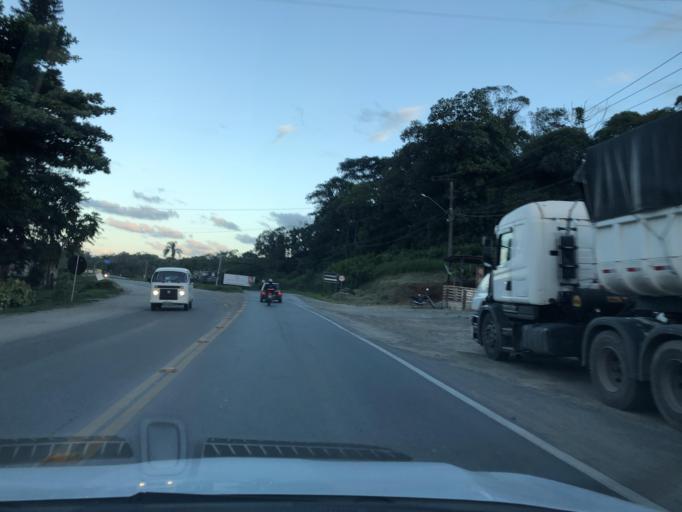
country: BR
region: Santa Catarina
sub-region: Sao Francisco Do Sul
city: Sao Francisco do Sul
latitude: -26.2535
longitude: -48.6142
